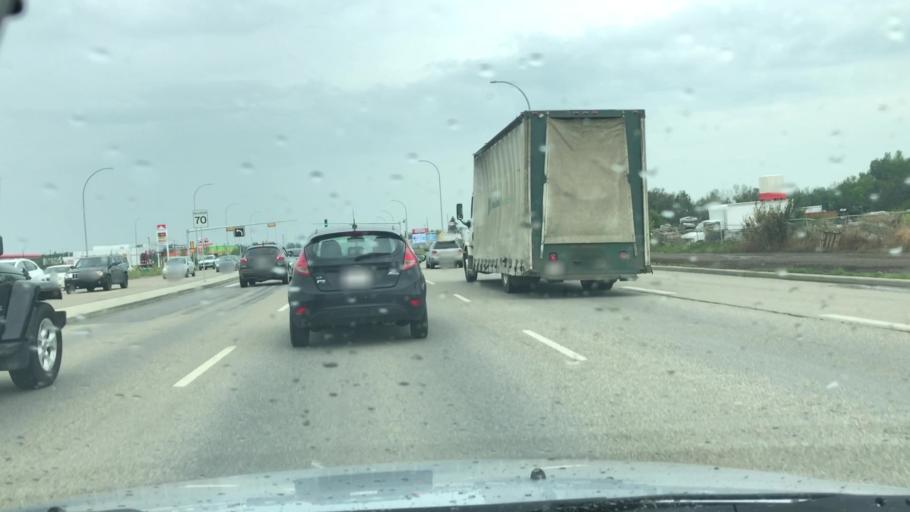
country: CA
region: Alberta
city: St. Albert
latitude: 53.6009
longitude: -113.5762
